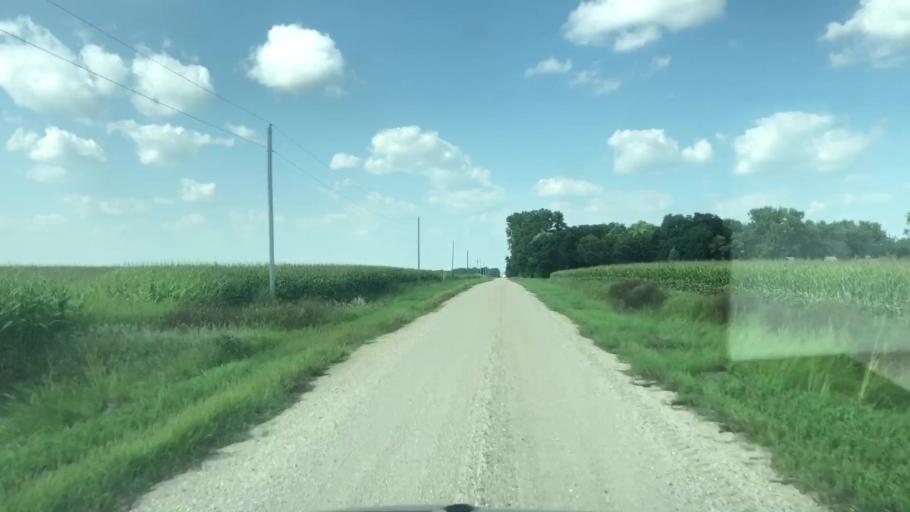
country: US
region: Iowa
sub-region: O'Brien County
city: Sheldon
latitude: 43.1603
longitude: -95.7822
